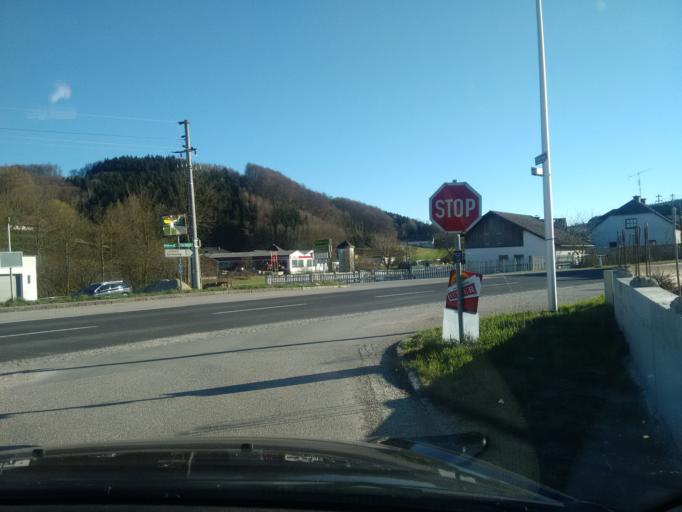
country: AT
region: Upper Austria
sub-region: Wels-Land
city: Offenhausen
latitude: 48.1518
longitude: 13.8333
